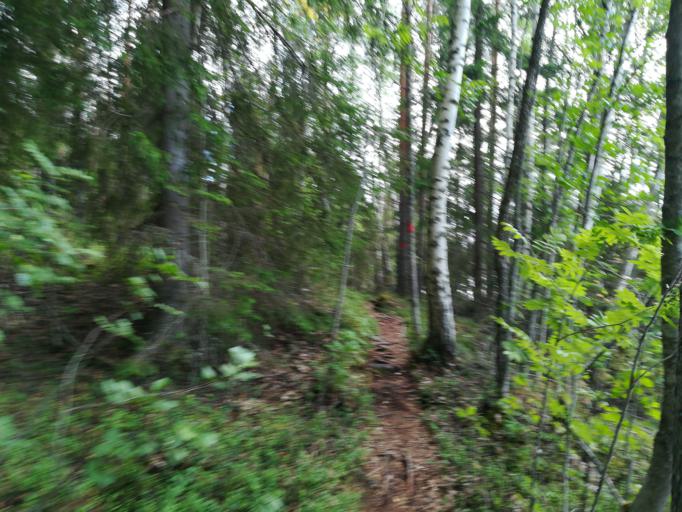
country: FI
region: South Karelia
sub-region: Lappeenranta
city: Savitaipale
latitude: 61.3059
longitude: 27.6146
